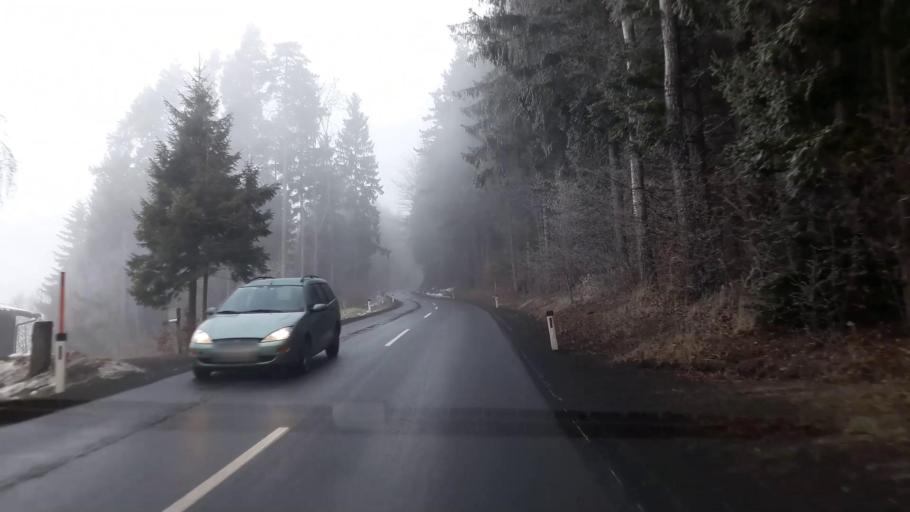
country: AT
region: Lower Austria
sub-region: Politischer Bezirk Neunkirchen
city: Feistritz am Wechsel
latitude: 47.5727
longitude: 16.0320
